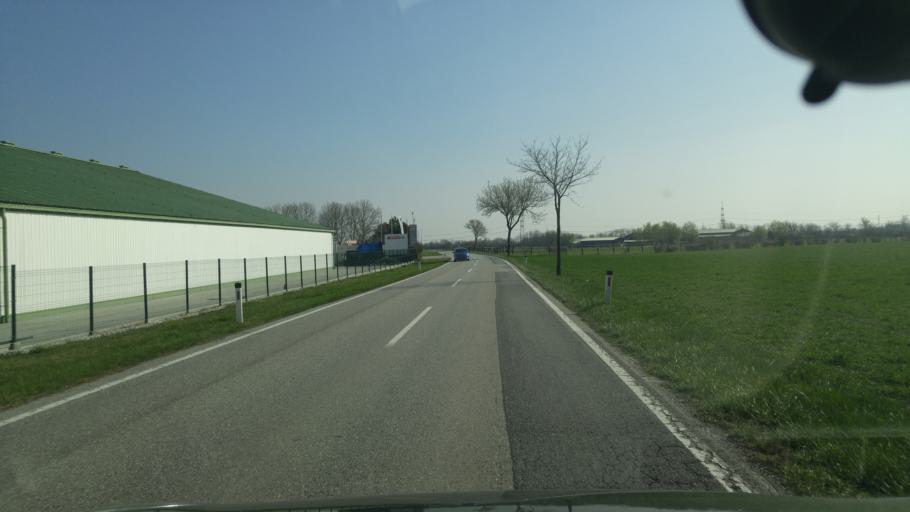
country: AT
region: Lower Austria
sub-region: Politischer Bezirk Baden
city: Trumau
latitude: 47.9928
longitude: 16.3573
